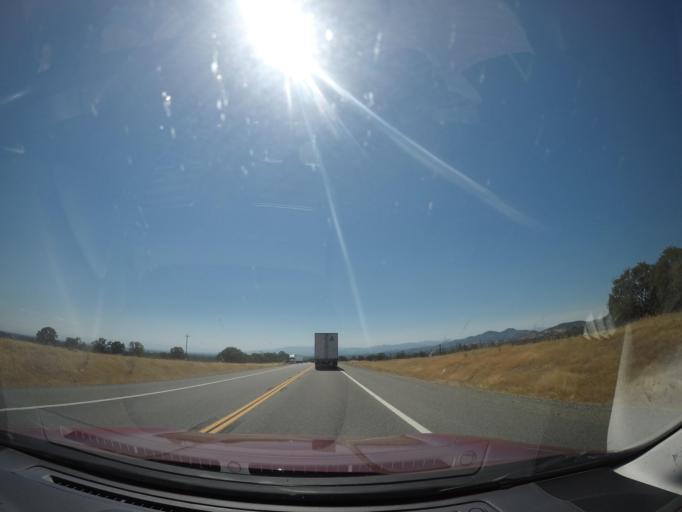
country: US
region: California
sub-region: Shasta County
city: Bella Vista
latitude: 40.6892
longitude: -122.1223
